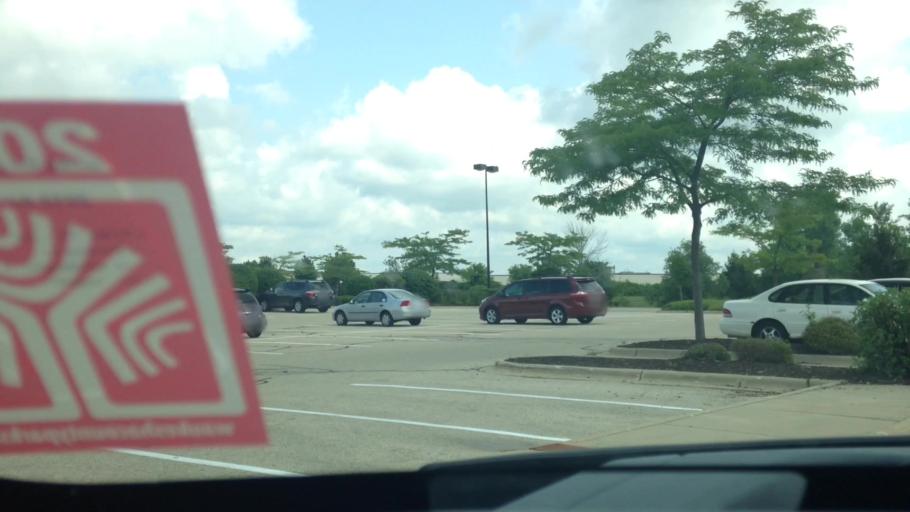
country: US
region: Wisconsin
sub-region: Waukesha County
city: Menomonee Falls
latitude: 43.1876
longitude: -88.1369
